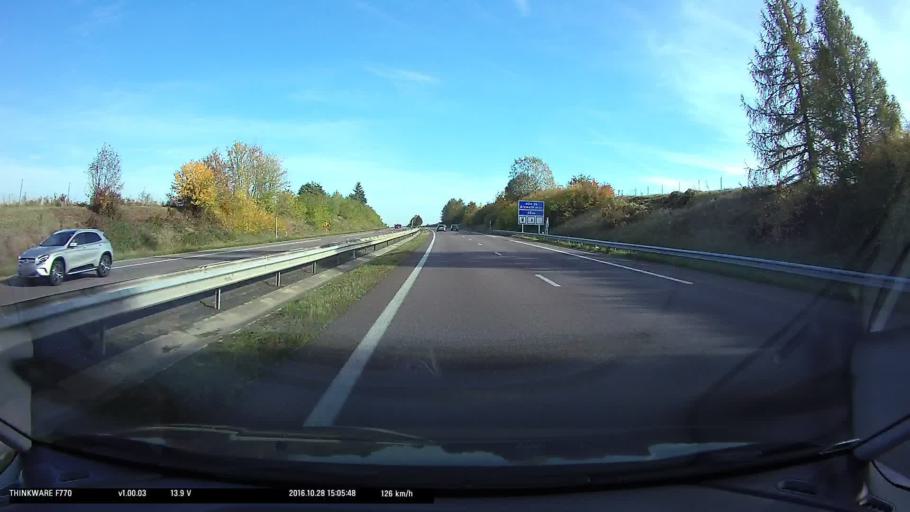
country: FR
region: Alsace
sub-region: Departement du Bas-Rhin
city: Dettwiller
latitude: 48.7709
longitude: 7.4671
